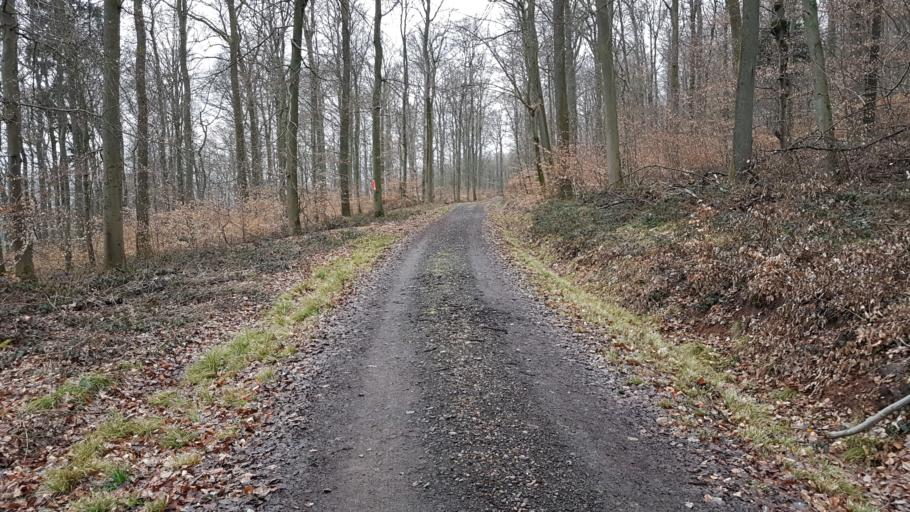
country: DE
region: Saarland
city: Sankt Wendel
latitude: 49.4387
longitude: 7.1790
